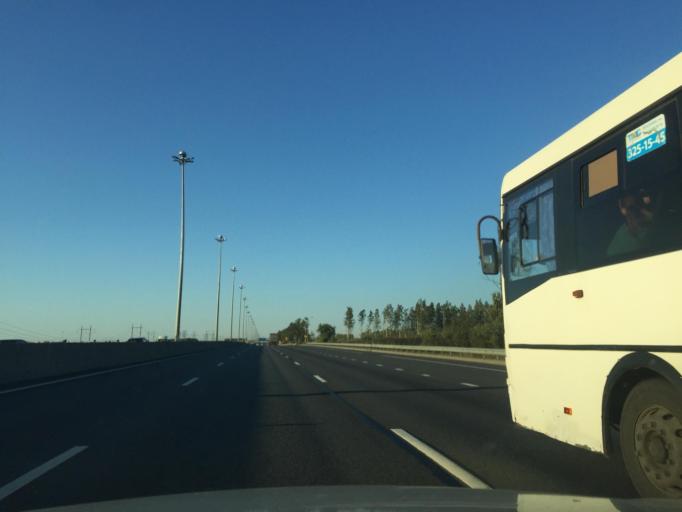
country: RU
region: St.-Petersburg
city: Aleksandrovskaya
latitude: 59.7060
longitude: 30.2696
